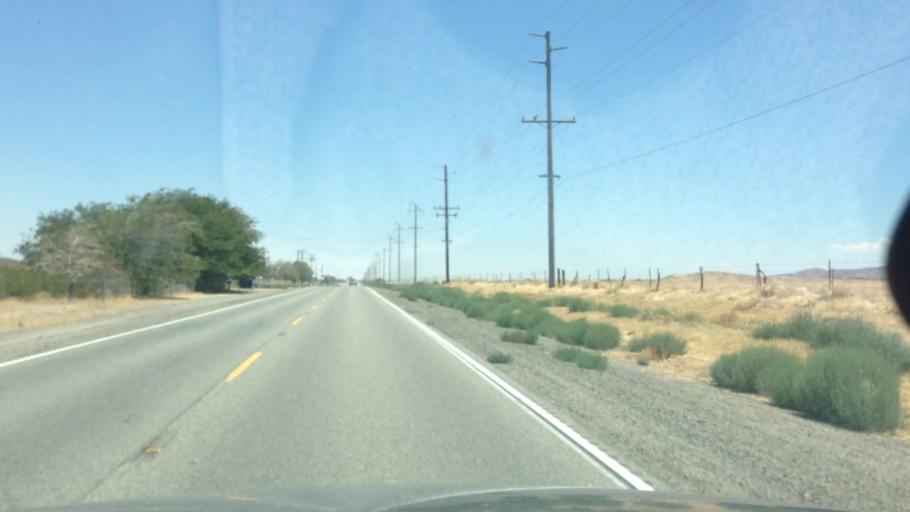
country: US
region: California
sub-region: Kern County
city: Lebec
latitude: 34.7833
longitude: -118.6326
